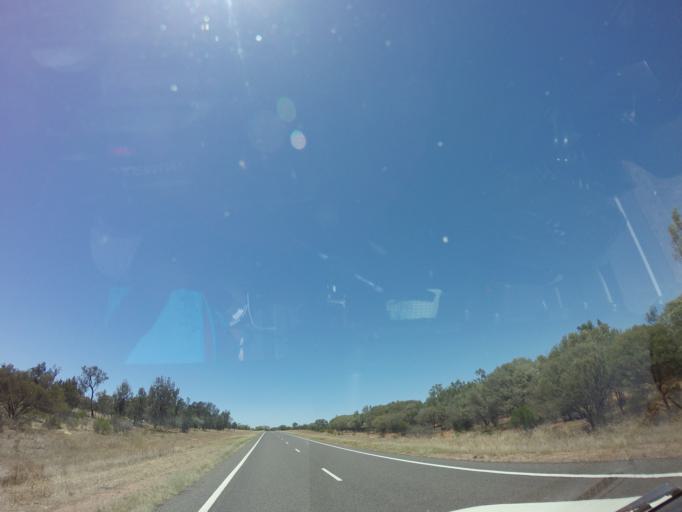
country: AU
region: New South Wales
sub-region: Cobar
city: Cobar
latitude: -31.5734
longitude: 144.7973
